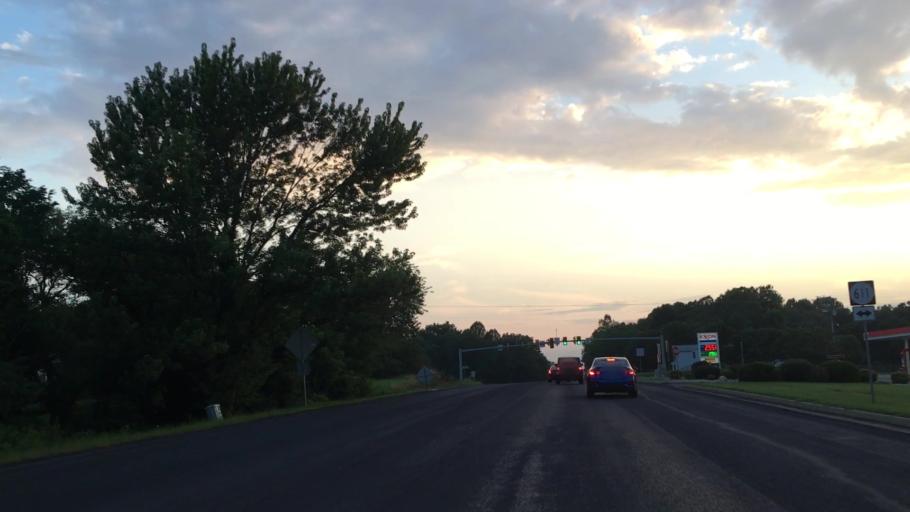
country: US
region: Virginia
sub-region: Spotsylvania County
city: Spotsylvania
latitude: 38.3053
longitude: -77.8088
